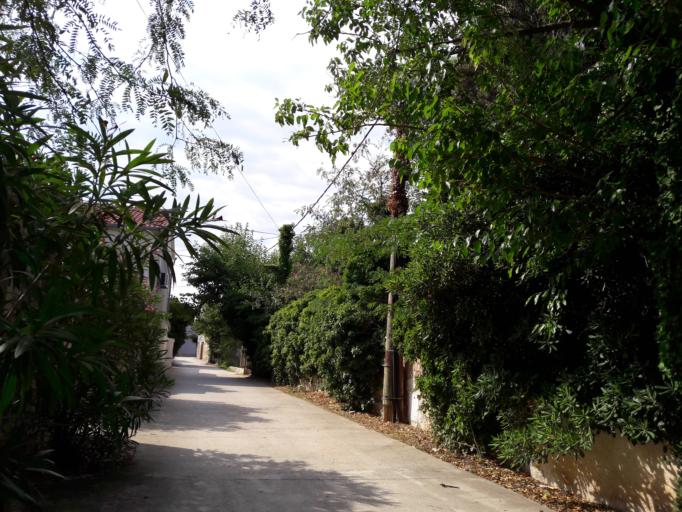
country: HR
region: Licko-Senjska
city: Novalja
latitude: 44.3775
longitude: 14.6935
